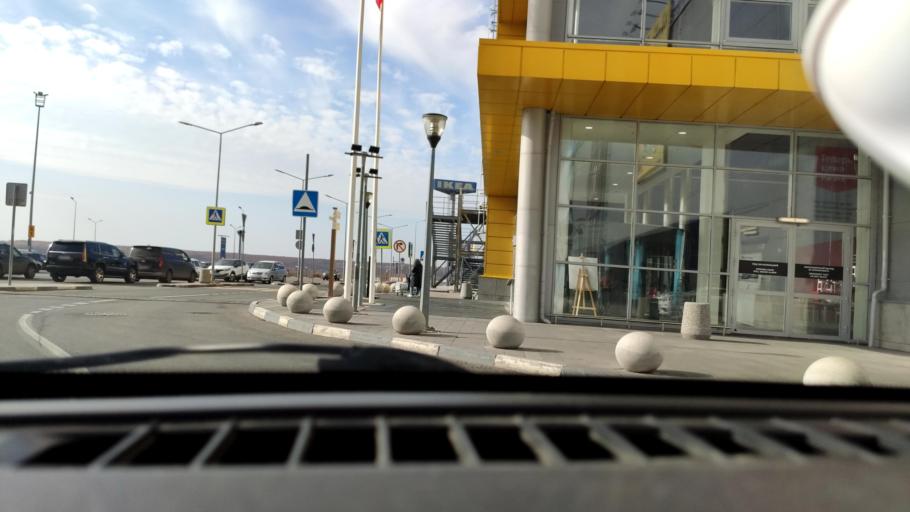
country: RU
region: Samara
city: Novosemeykino
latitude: 53.3251
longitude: 50.3037
